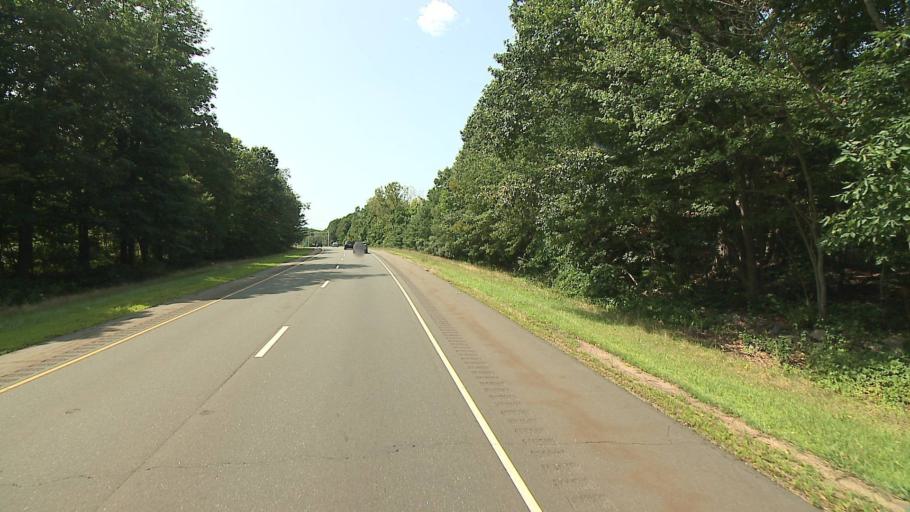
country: US
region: Connecticut
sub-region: Fairfield County
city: Trumbull
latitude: 41.2866
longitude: -73.2303
